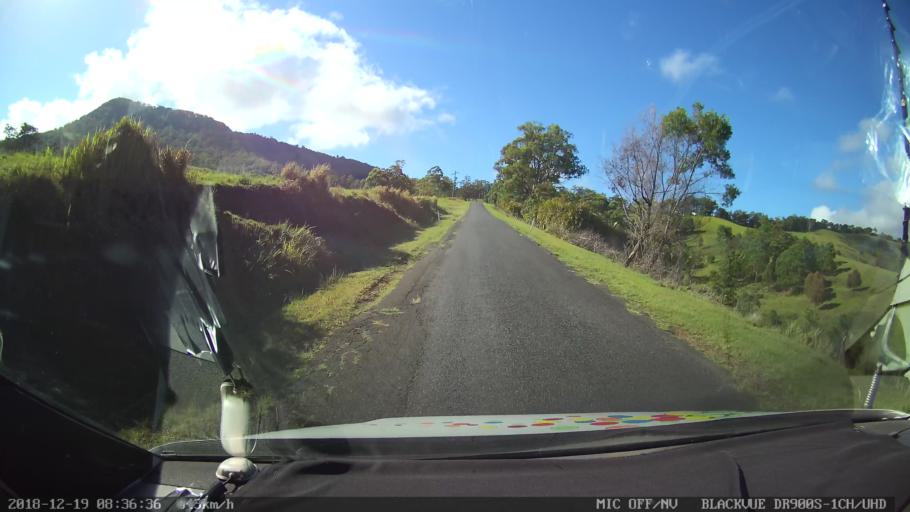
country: AU
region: New South Wales
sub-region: Kyogle
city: Kyogle
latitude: -28.3266
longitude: 152.9731
